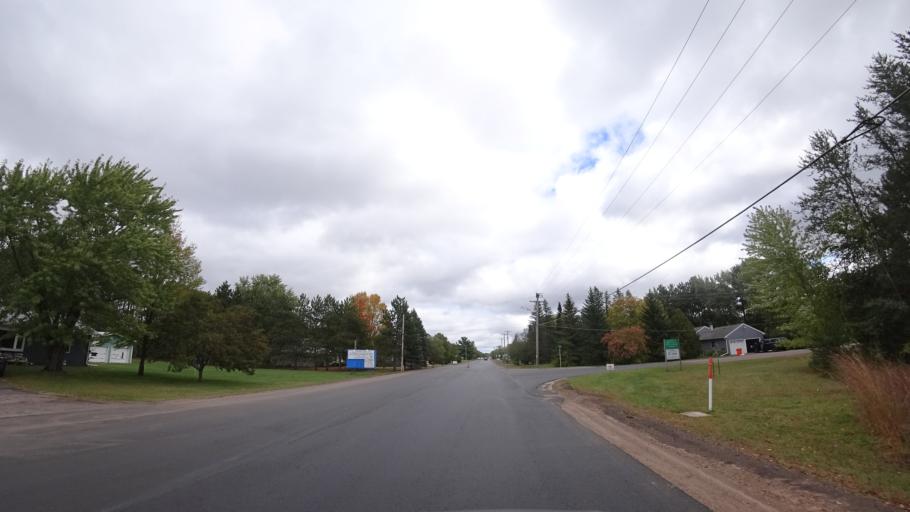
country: US
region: Wisconsin
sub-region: Chippewa County
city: Lake Wissota
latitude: 44.9296
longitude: -91.2748
